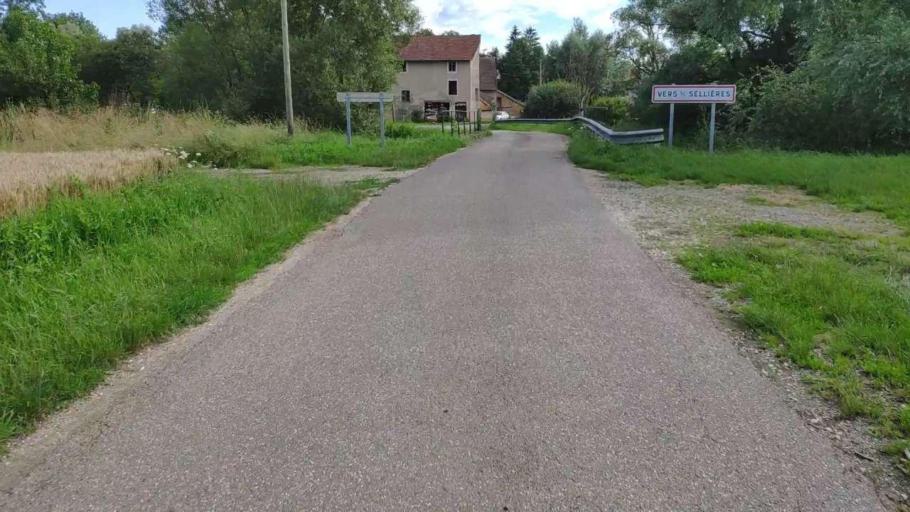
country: FR
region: Franche-Comte
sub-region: Departement du Jura
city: Bletterans
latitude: 46.8275
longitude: 5.5379
